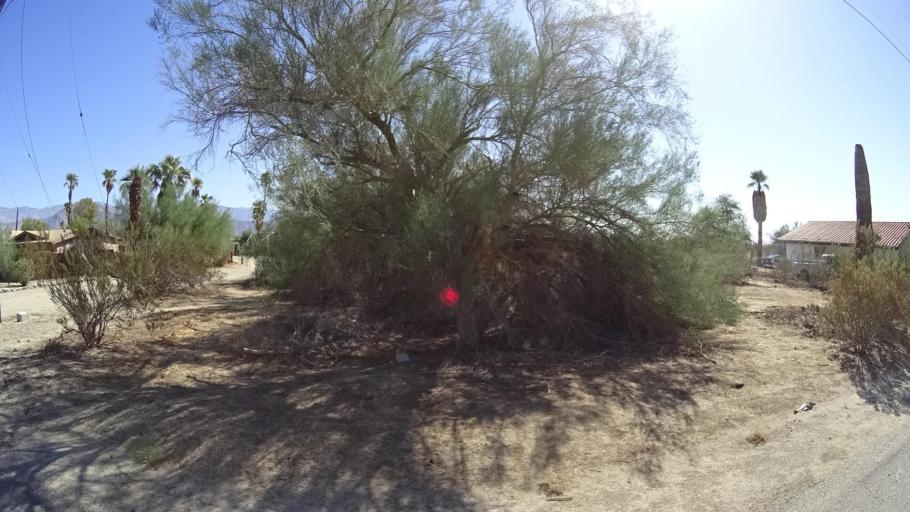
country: US
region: California
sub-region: San Diego County
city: Borrego Springs
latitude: 33.2732
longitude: -116.3912
